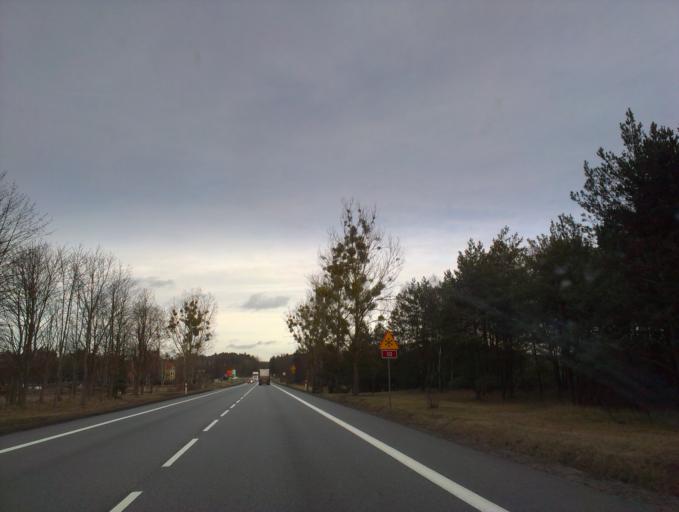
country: PL
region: Kujawsko-Pomorskie
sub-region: Powiat lipnowski
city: Skepe
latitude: 52.8801
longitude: 19.3797
